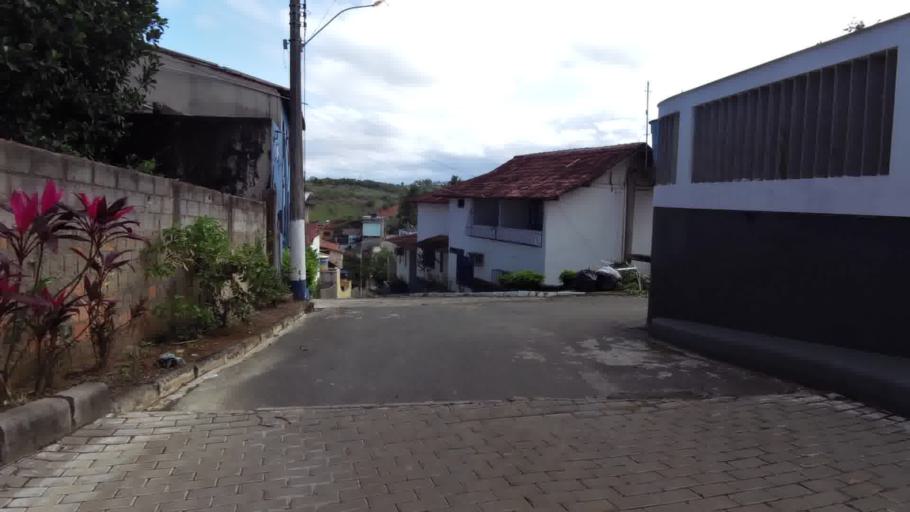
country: BR
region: Espirito Santo
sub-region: Piuma
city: Piuma
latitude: -20.8322
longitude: -40.6990
